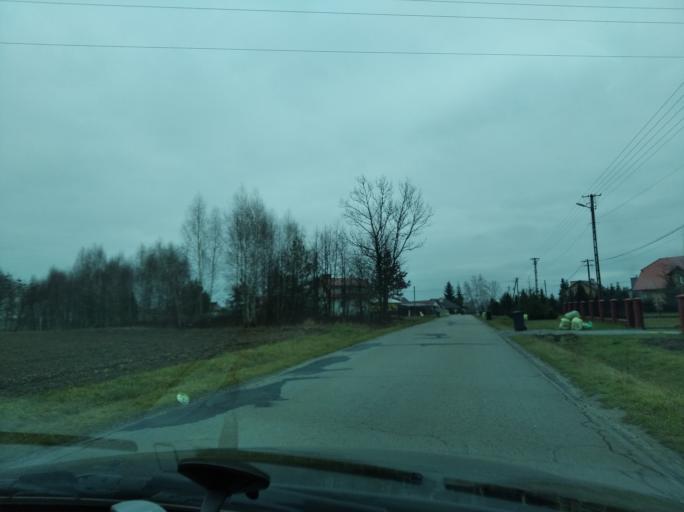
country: PL
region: Subcarpathian Voivodeship
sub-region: Powiat lancucki
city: Zolynia
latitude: 50.1810
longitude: 22.3103
